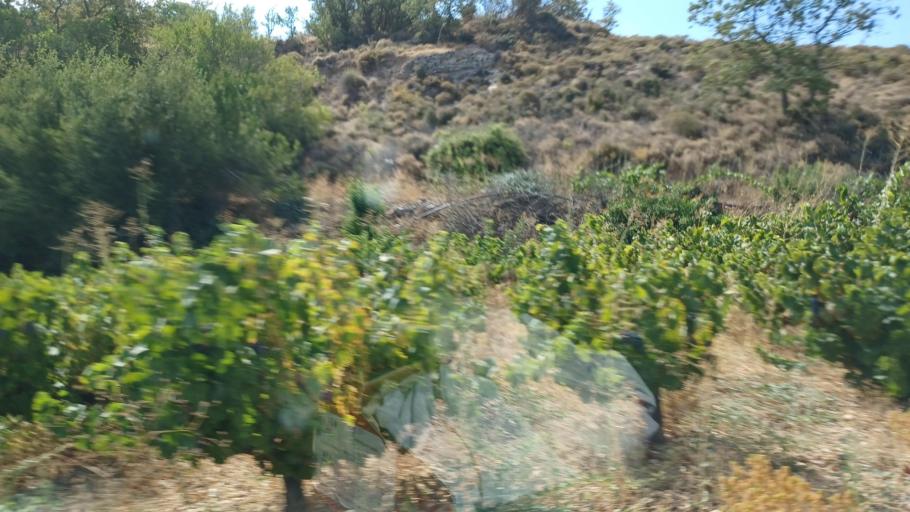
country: CY
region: Pafos
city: Mesogi
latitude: 34.8807
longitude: 32.6104
